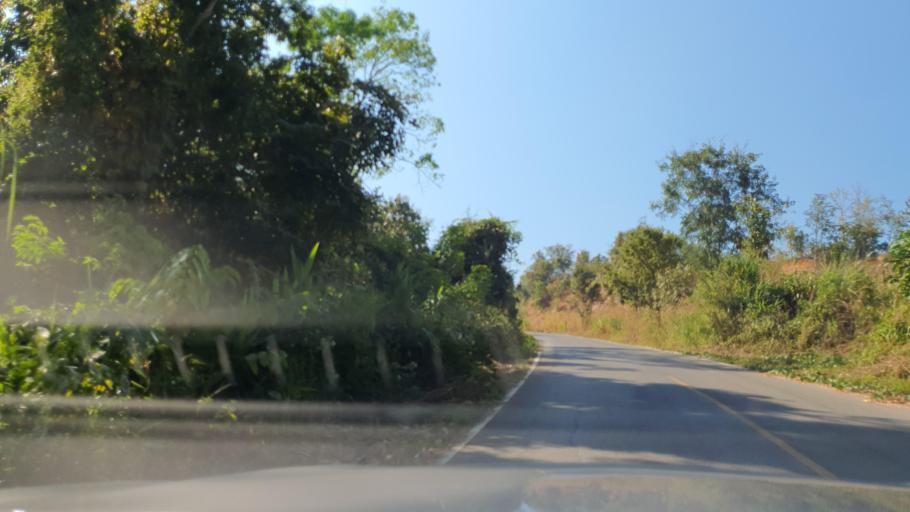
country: TH
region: Nan
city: Pua
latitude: 19.1613
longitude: 100.9072
